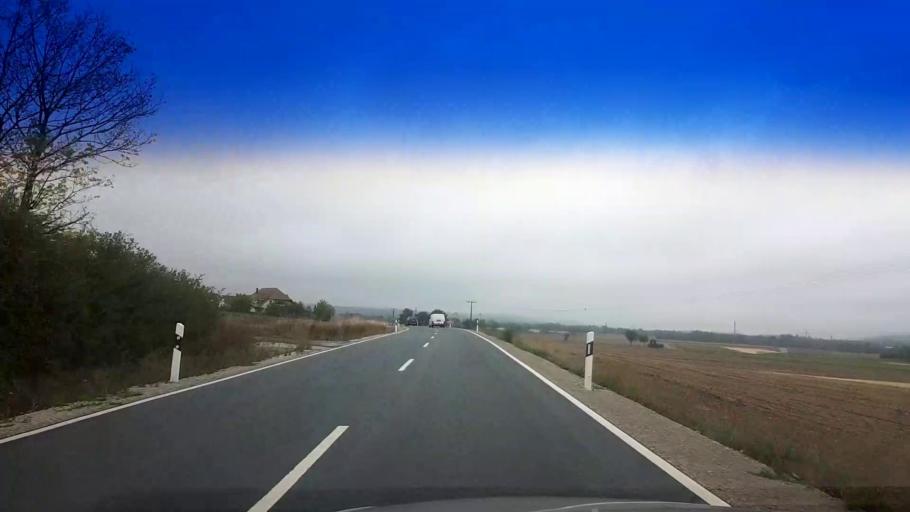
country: DE
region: Bavaria
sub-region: Upper Franconia
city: Buttenheim
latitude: 49.7896
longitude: 11.0399
